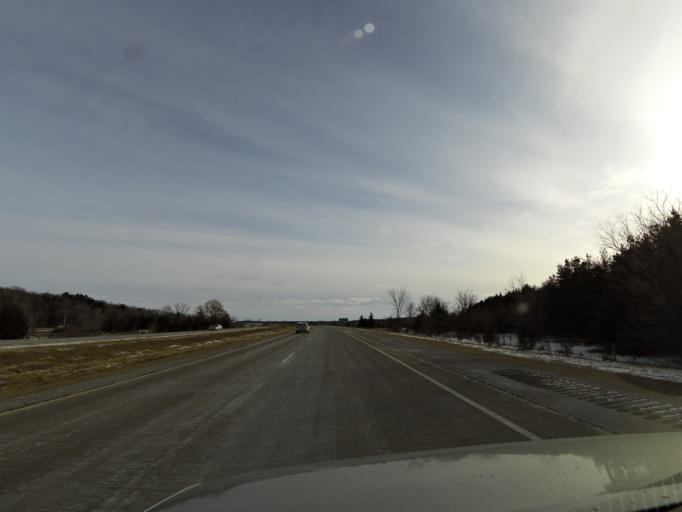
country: US
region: Wisconsin
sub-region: Saint Croix County
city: Hudson
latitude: 44.9385
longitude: -92.6927
